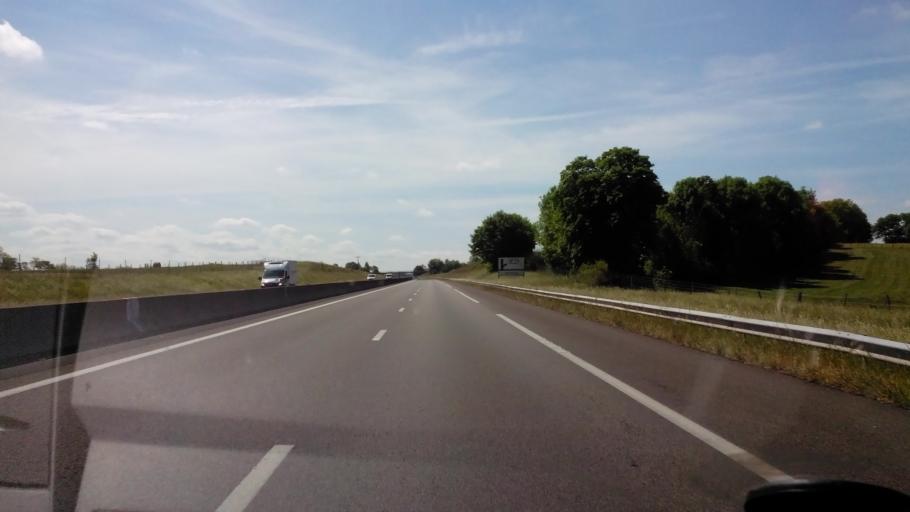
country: FR
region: Lorraine
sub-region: Departement de Meurthe-et-Moselle
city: Colombey-les-Belles
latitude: 48.5586
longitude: 5.8911
